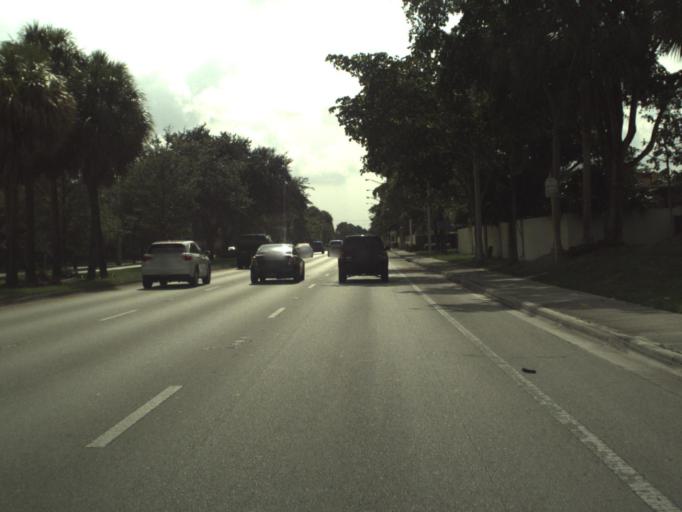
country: US
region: Florida
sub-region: Broward County
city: Plantation
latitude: 26.1485
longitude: -80.2491
